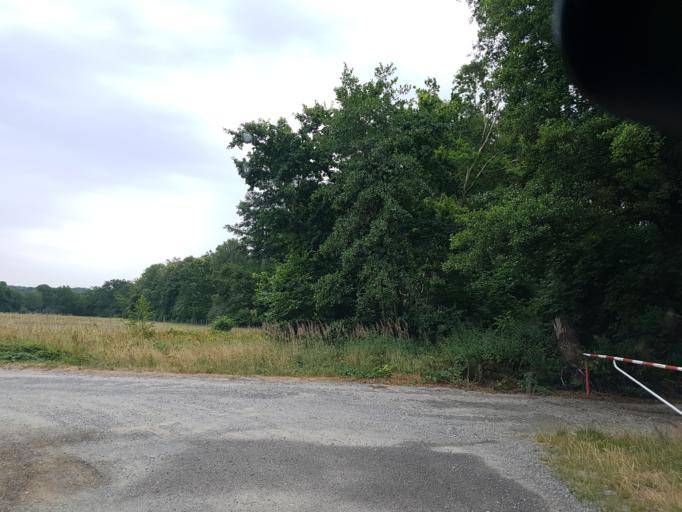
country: DE
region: Brandenburg
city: Sallgast
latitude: 51.5656
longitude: 13.8584
